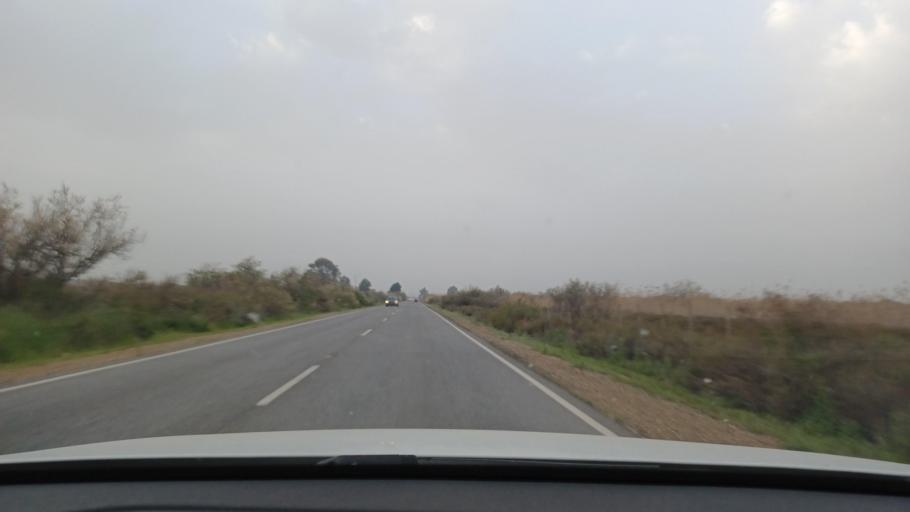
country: ES
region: Valencia
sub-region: Provincia de Alicante
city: Dolores
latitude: 38.1740
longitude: -0.7021
